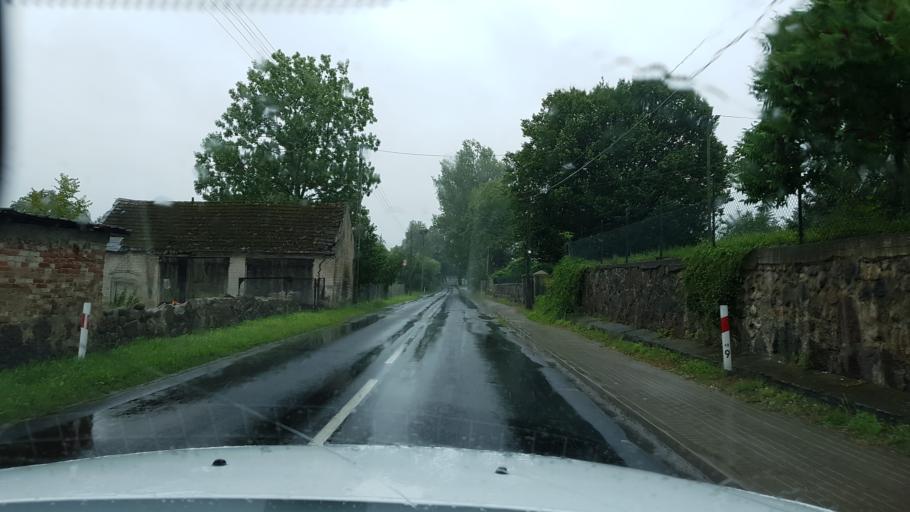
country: PL
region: West Pomeranian Voivodeship
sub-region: Powiat goleniowski
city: Nowogard
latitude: 53.5896
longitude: 15.1472
